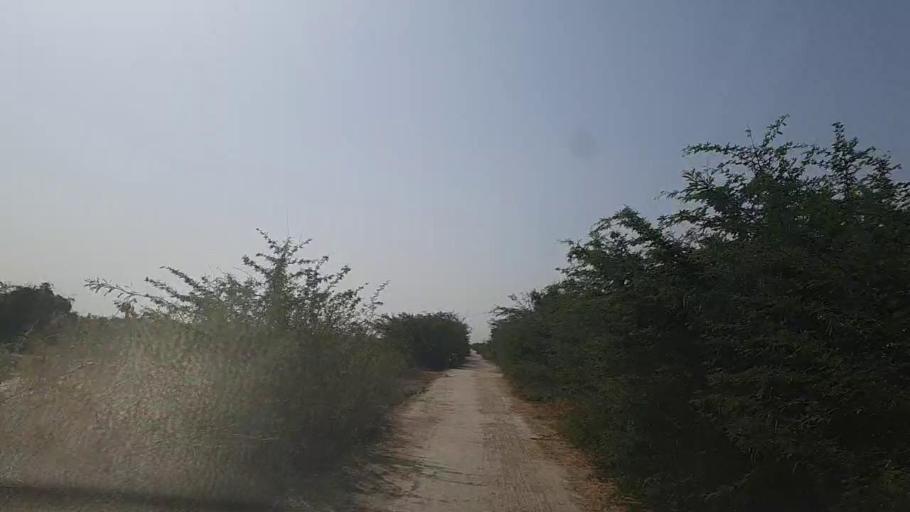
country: PK
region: Sindh
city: Naukot
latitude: 24.5689
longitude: 69.2879
